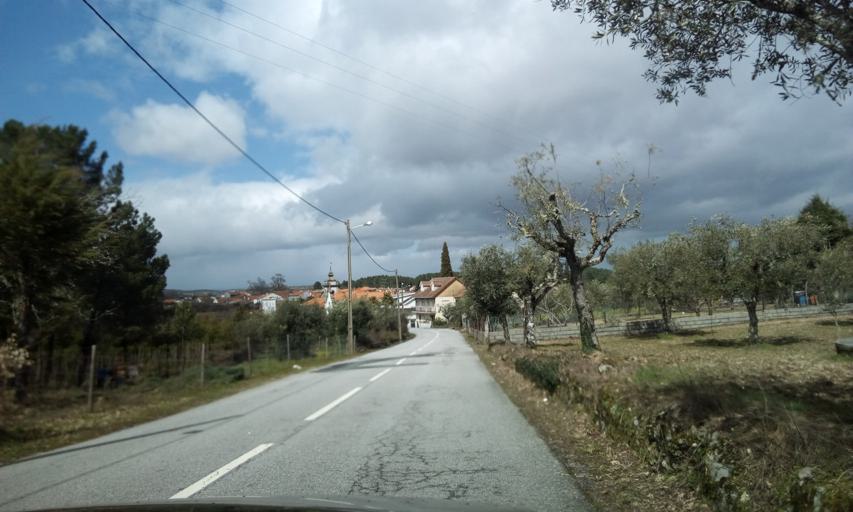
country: PT
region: Guarda
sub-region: Fornos de Algodres
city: Fornos de Algodres
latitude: 40.6447
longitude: -7.5478
